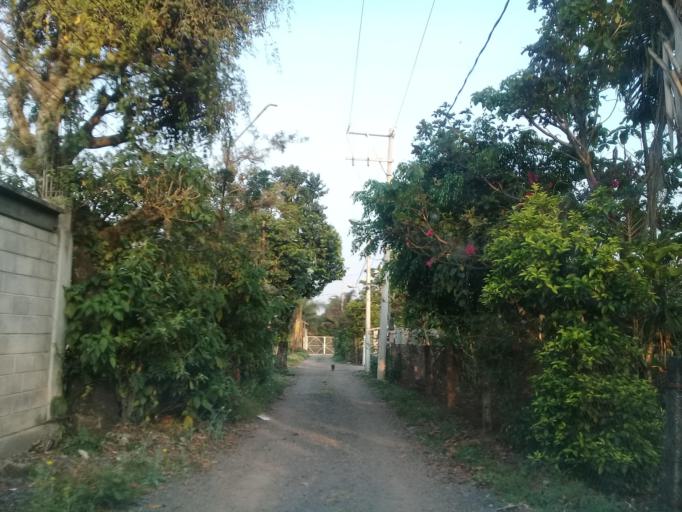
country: MX
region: Veracruz
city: Ixtac Zoquitlan
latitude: 18.8471
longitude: -97.0568
